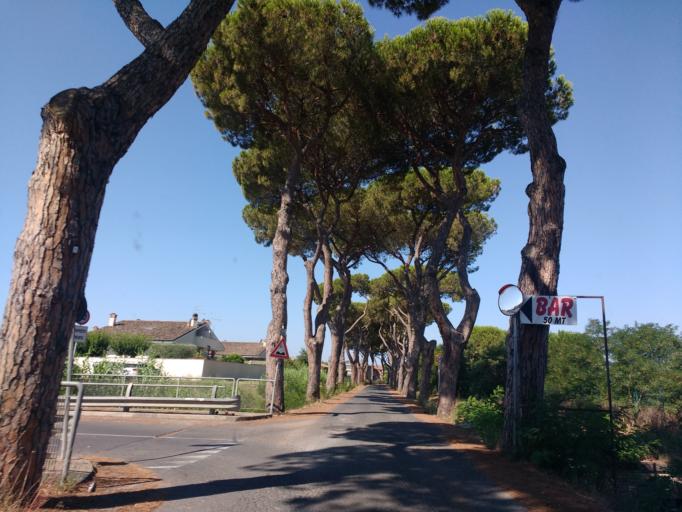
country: IT
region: Latium
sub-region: Citta metropolitana di Roma Capitale
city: Acilia-Castel Fusano-Ostia Antica
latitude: 41.7529
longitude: 12.3368
